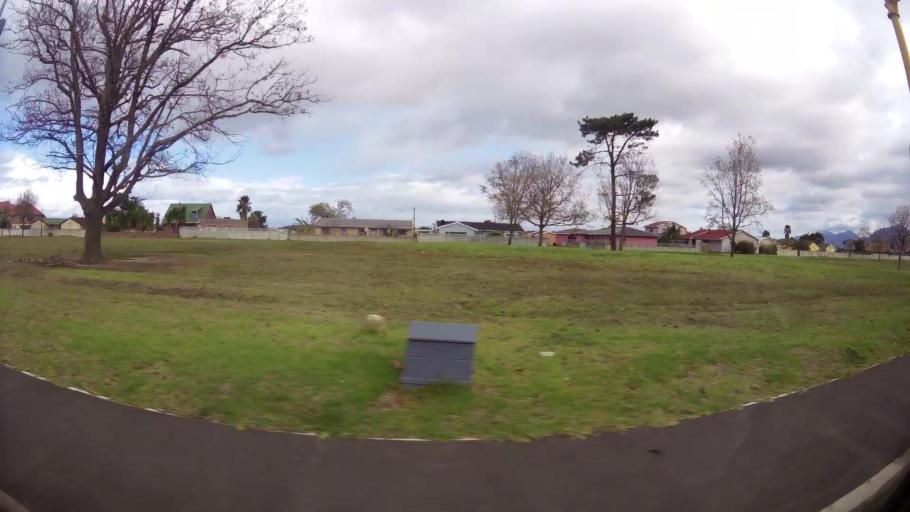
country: ZA
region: Western Cape
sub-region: Eden District Municipality
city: George
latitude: -33.9687
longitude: 22.4872
